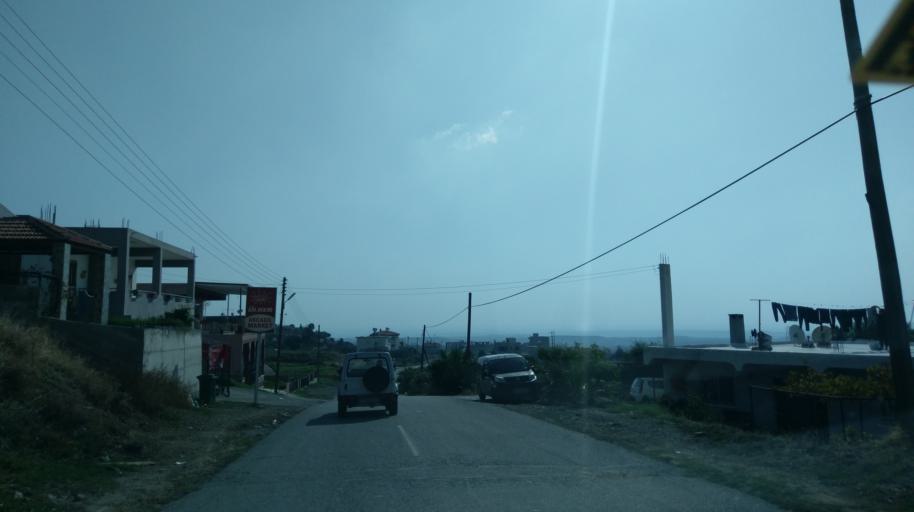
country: CY
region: Ammochostos
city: Lefkonoiko
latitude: 35.2784
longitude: 33.5786
